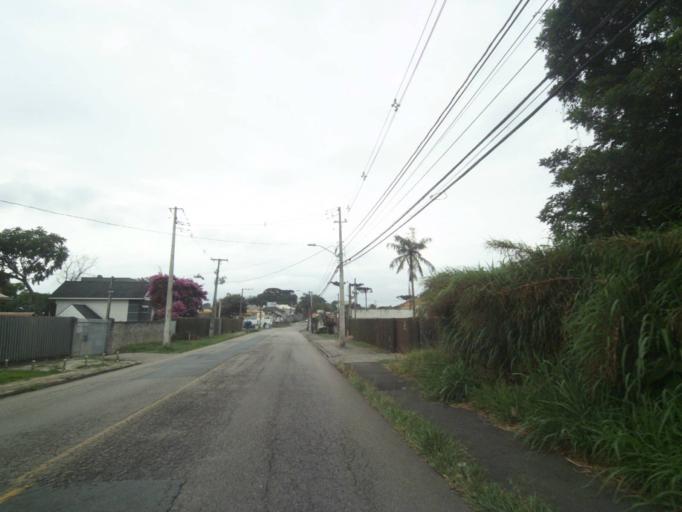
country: BR
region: Parana
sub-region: Curitiba
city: Curitiba
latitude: -25.4062
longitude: -49.3135
